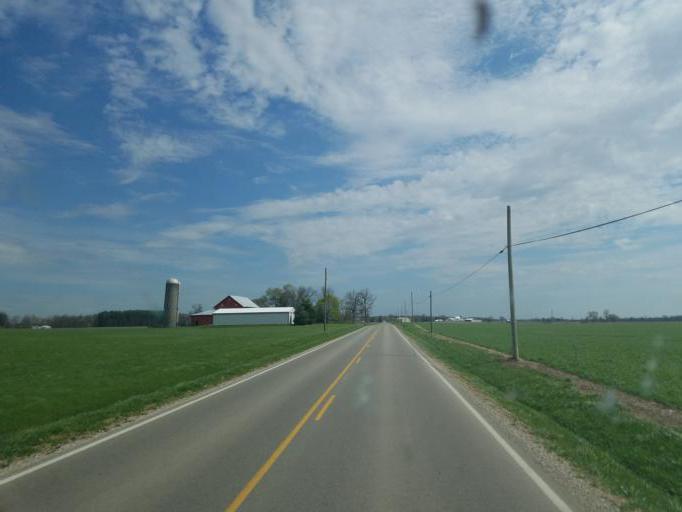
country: US
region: Ohio
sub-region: Crawford County
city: Bucyrus
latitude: 40.7789
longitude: -83.0263
